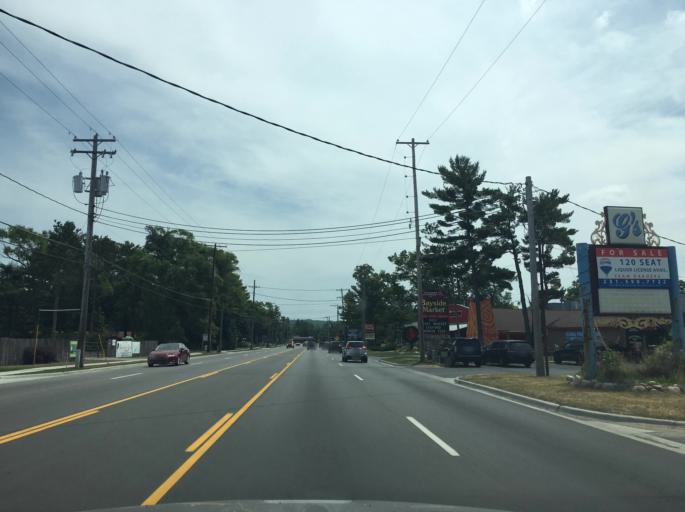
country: US
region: Michigan
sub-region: Grand Traverse County
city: Traverse City
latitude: 44.7465
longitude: -85.5464
